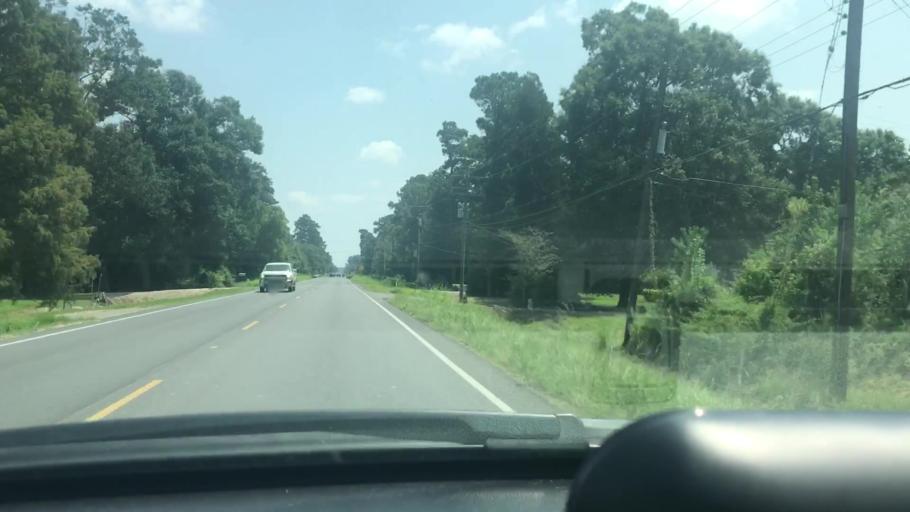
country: US
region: Louisiana
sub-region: Livingston Parish
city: Walker
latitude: 30.4847
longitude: -90.8956
